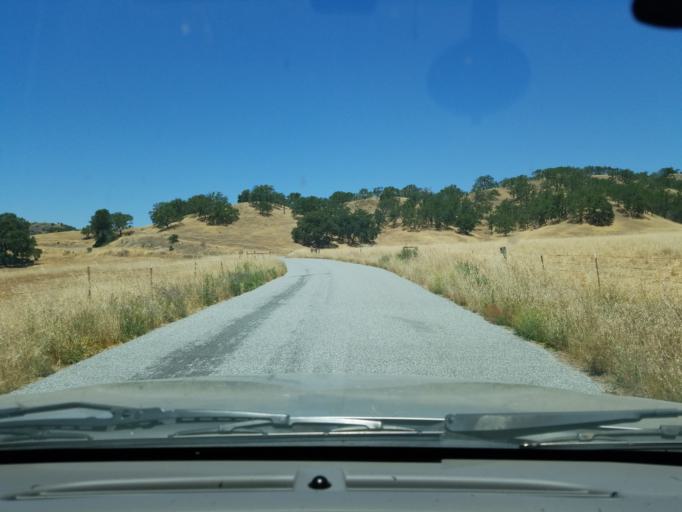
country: US
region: California
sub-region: Monterey County
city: Gonzales
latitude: 36.3947
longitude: -121.5719
